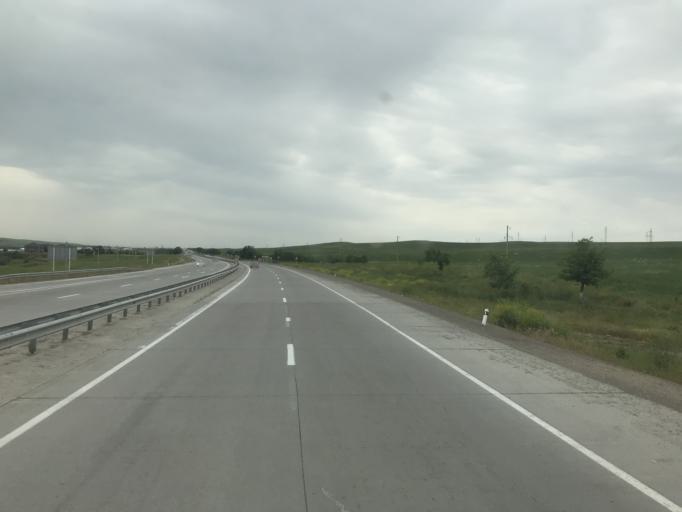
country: KZ
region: Ongtustik Qazaqstan
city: Qazyqurt
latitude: 41.8620
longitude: 69.4111
